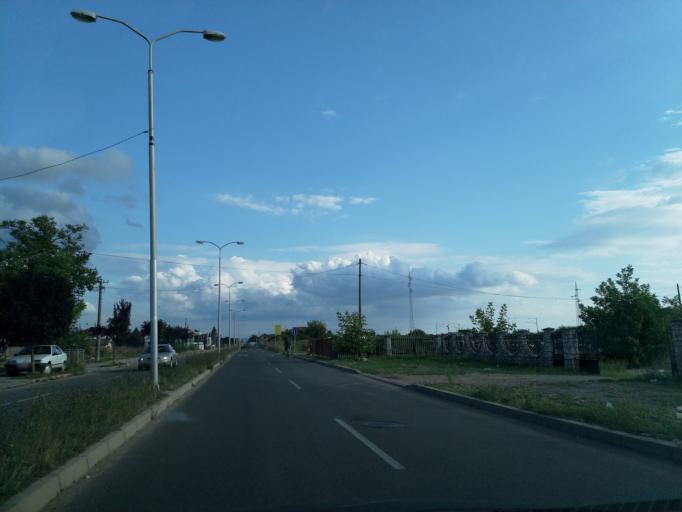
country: RS
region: Central Serbia
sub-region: Pomoravski Okrug
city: Paracin
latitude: 43.8463
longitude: 21.4141
